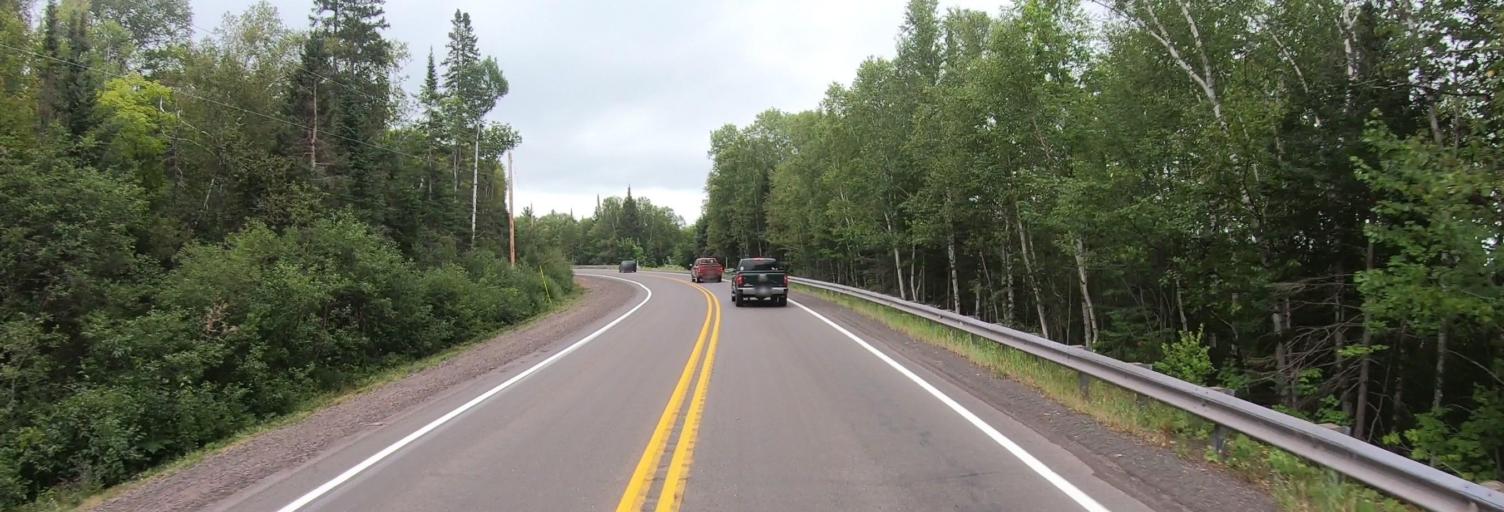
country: US
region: Michigan
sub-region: Keweenaw County
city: Eagle River
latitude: 47.4165
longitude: -88.1473
